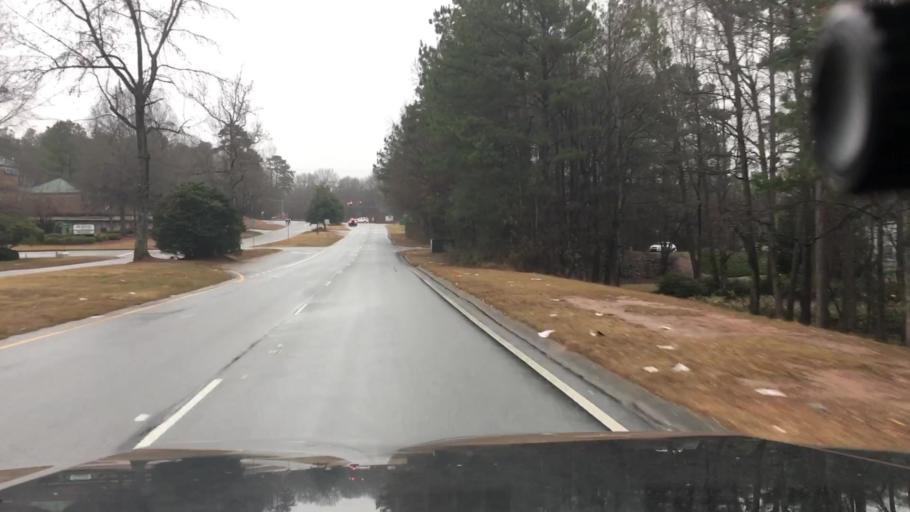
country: US
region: Georgia
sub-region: Coweta County
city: East Newnan
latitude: 33.3967
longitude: -84.7326
